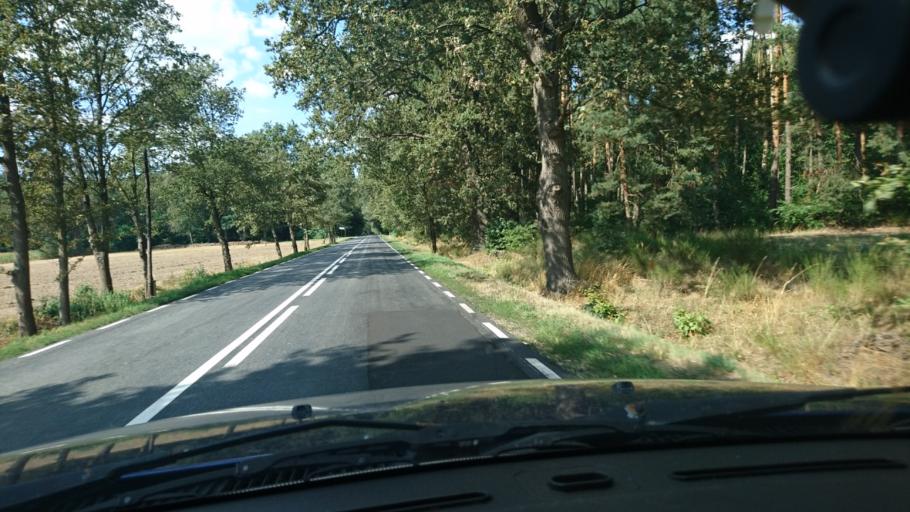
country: PL
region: Greater Poland Voivodeship
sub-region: Powiat krotoszynski
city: Sulmierzyce
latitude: 51.6227
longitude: 17.4996
